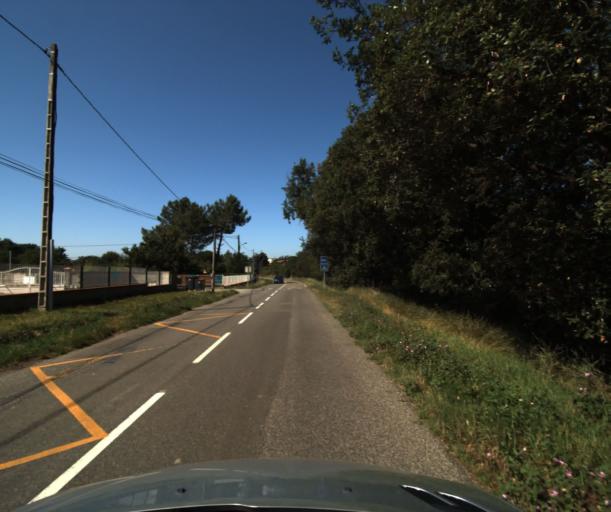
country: FR
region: Midi-Pyrenees
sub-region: Departement de la Haute-Garonne
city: Saubens
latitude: 43.4935
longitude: 1.3543
